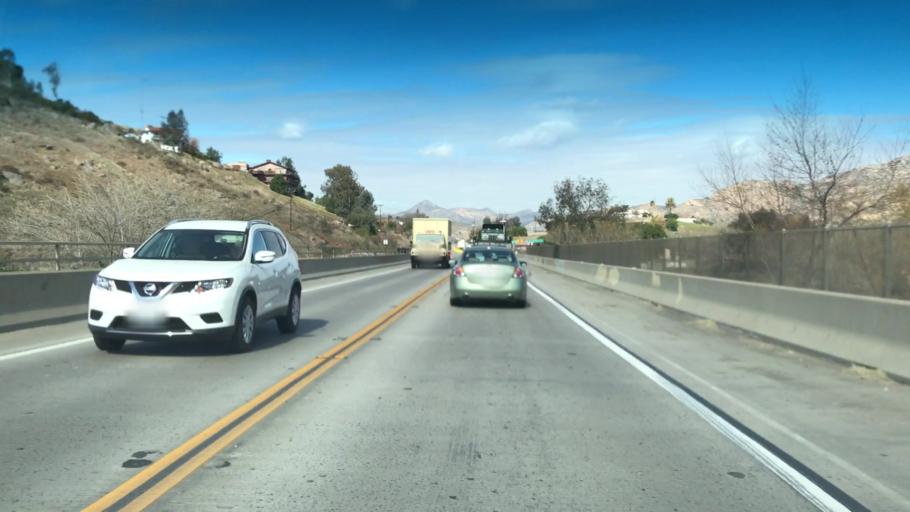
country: US
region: California
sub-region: San Diego County
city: Lakeside
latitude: 32.8699
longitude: -116.9232
